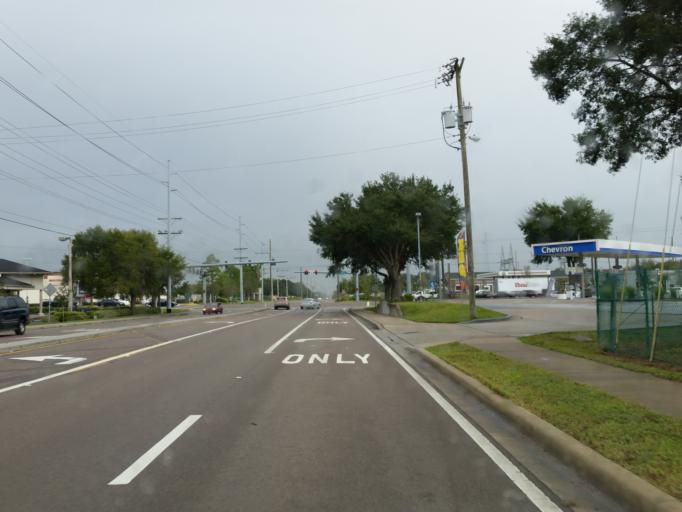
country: US
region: Florida
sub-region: Hillsborough County
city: Riverview
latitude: 27.8524
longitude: -82.3021
